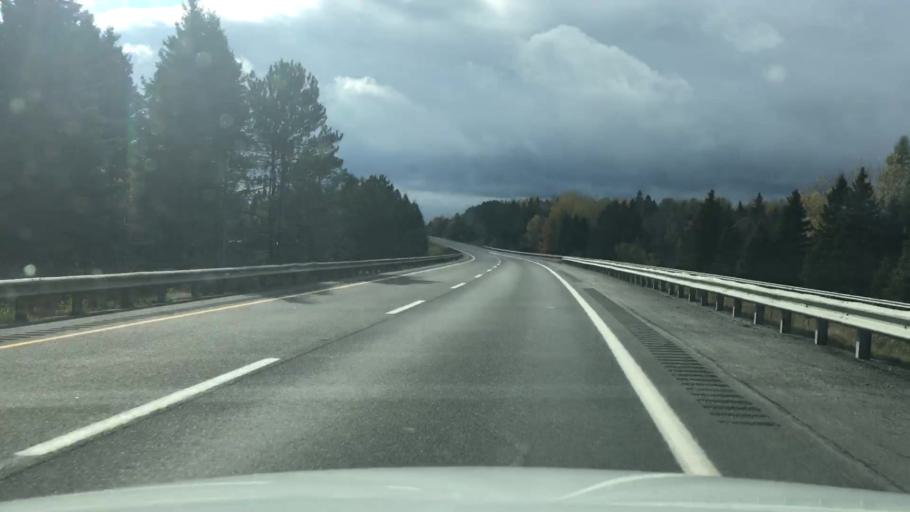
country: US
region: Maine
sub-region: Aroostook County
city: Hodgdon
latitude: 46.1100
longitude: -68.1625
